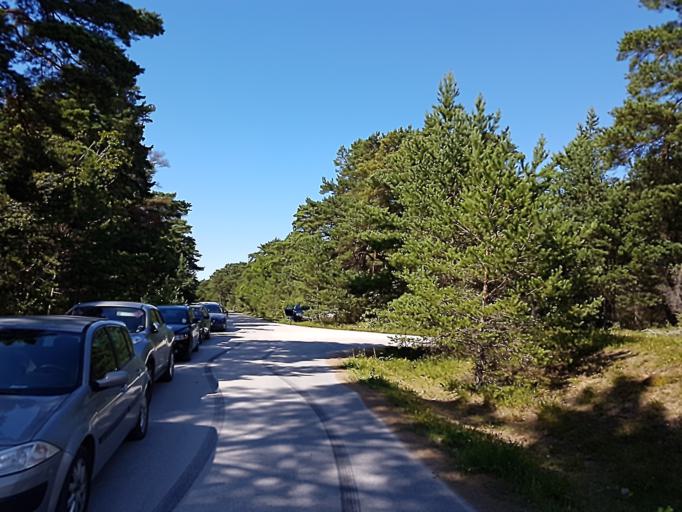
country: SE
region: Gotland
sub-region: Gotland
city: Visby
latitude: 57.6047
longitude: 18.3512
